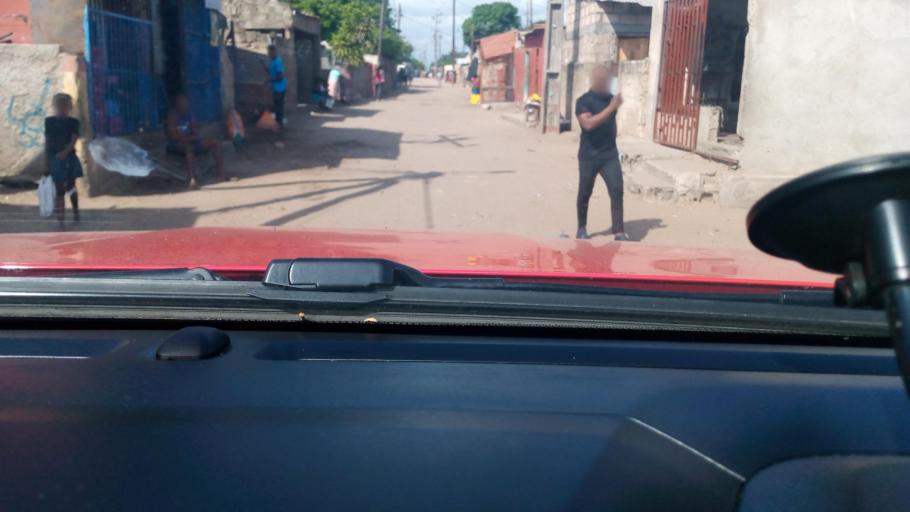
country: MZ
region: Maputo City
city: Maputo
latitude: -25.9149
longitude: 32.5631
